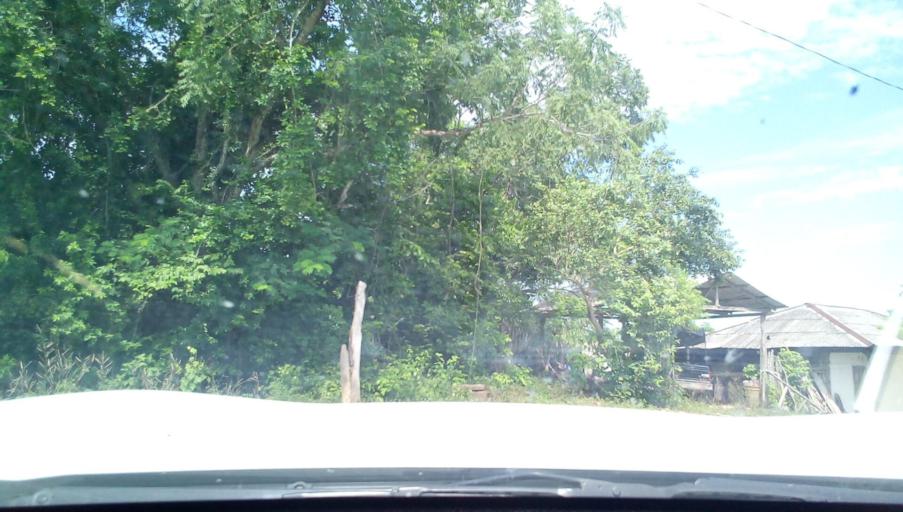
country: MX
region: Veracruz
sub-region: Alamo Temapache
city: Vegas de la Soledad y Soledad Dos
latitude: 20.8960
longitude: -97.9450
